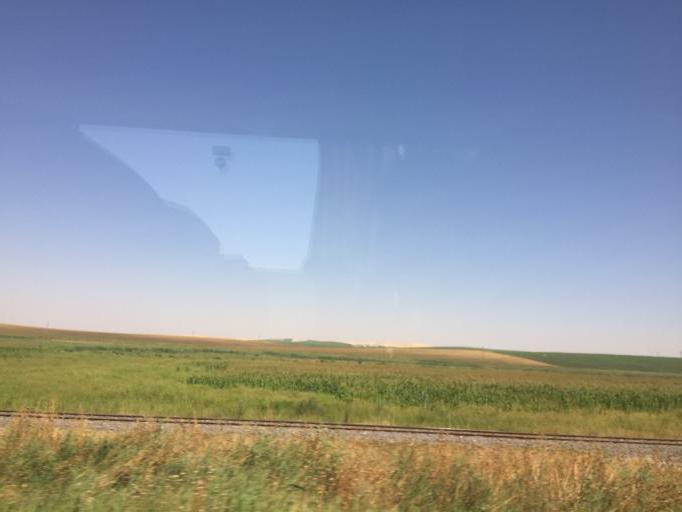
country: TR
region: Diyarbakir
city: Tepe
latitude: 37.8503
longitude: 40.7397
